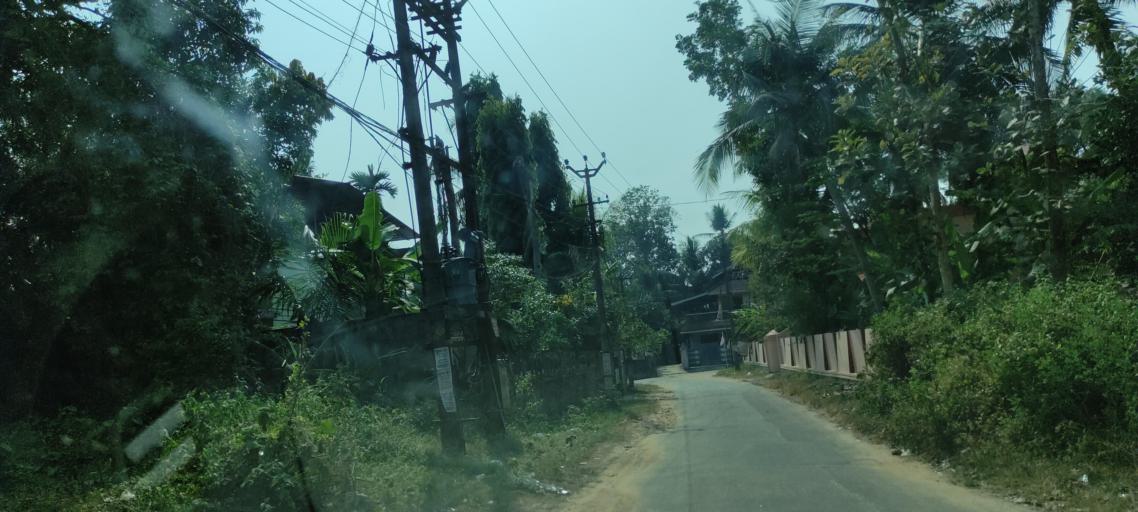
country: IN
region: Kerala
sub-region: Pattanamtitta
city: Tiruvalla
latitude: 9.3479
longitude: 76.5282
